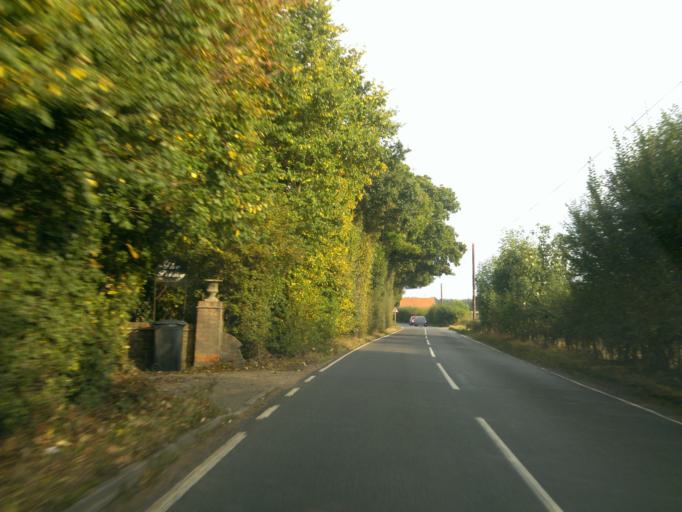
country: GB
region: England
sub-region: Essex
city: Tiptree
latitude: 51.7980
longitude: 0.7168
